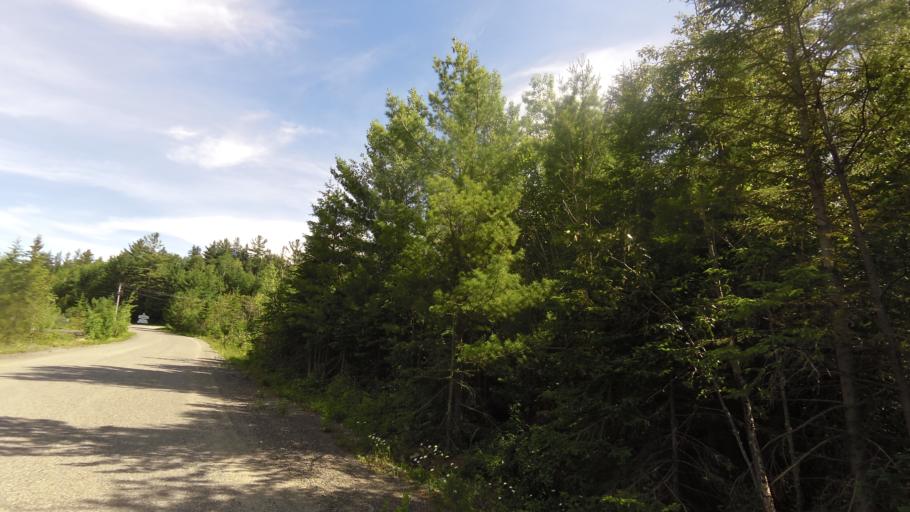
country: CA
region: Ontario
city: Temiskaming Shores
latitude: 47.3882
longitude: -79.6874
